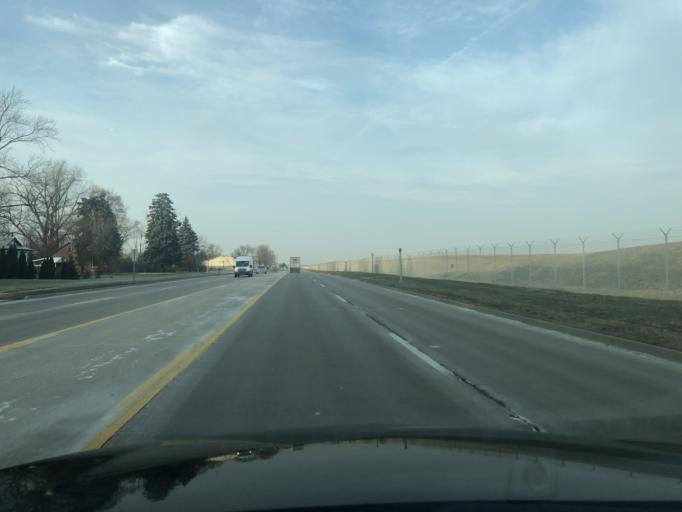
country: US
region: Michigan
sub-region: Wayne County
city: Romulus
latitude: 42.1955
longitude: -83.3293
